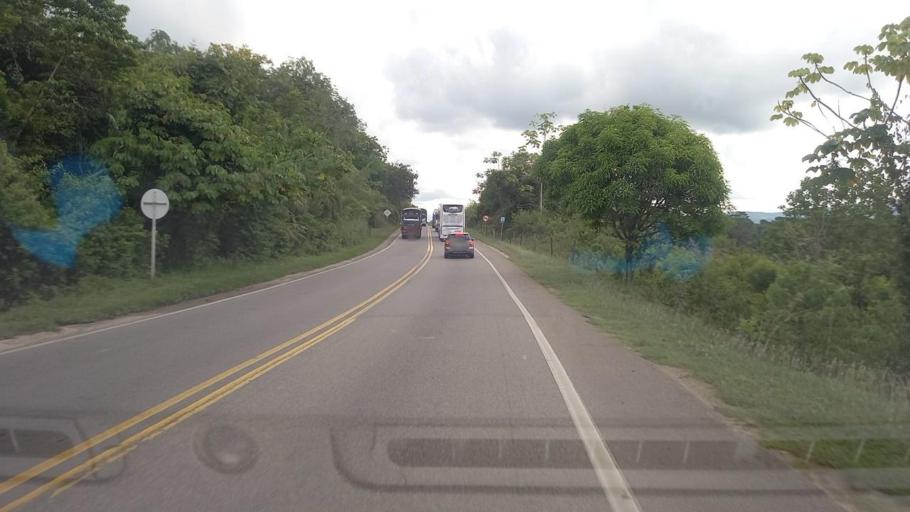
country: CO
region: Santander
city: Barrancabermeja
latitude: 7.1197
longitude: -73.6003
